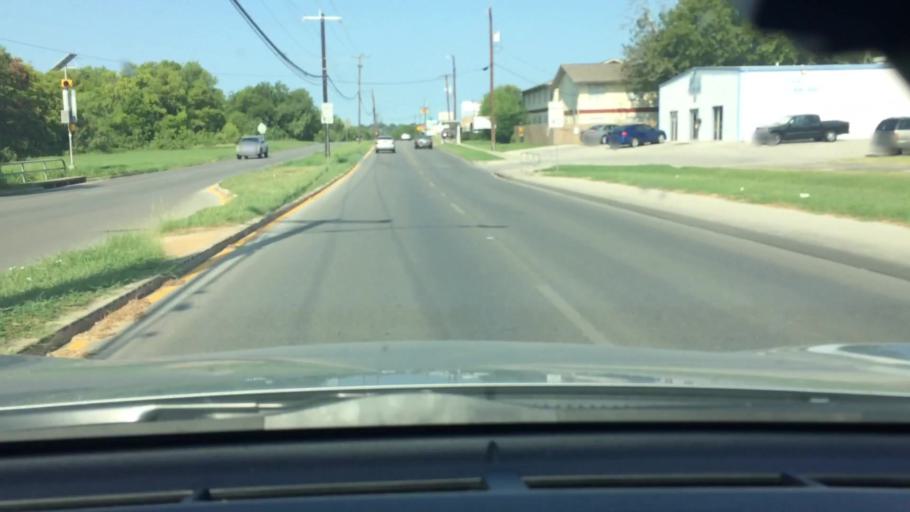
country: US
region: Texas
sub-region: Bexar County
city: China Grove
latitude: 29.3748
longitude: -98.4168
